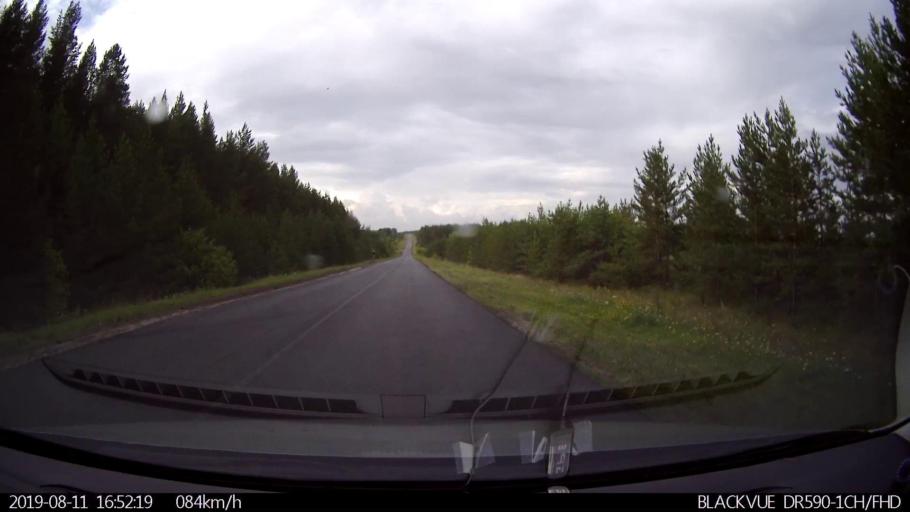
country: RU
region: Ulyanovsk
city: Mayna
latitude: 54.2467
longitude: 47.6745
